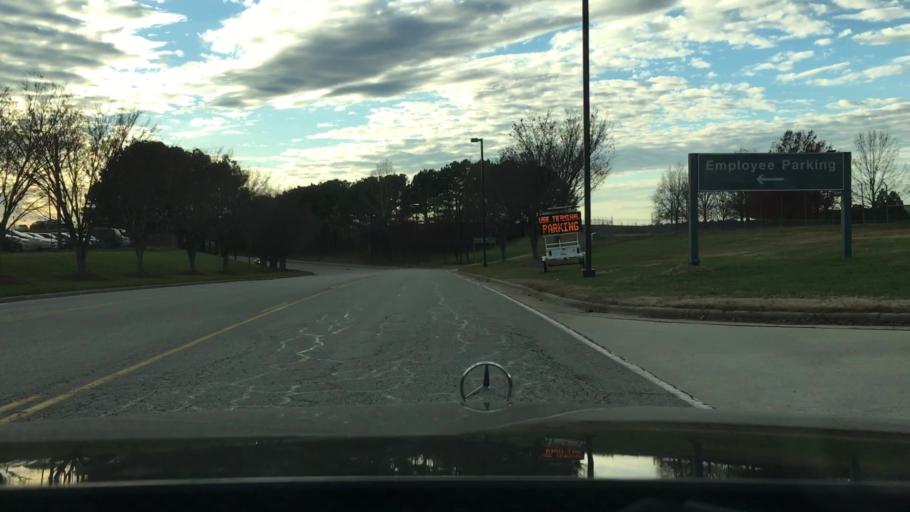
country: US
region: North Carolina
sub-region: Wake County
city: Morrisville
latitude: 35.8907
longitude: -78.7718
